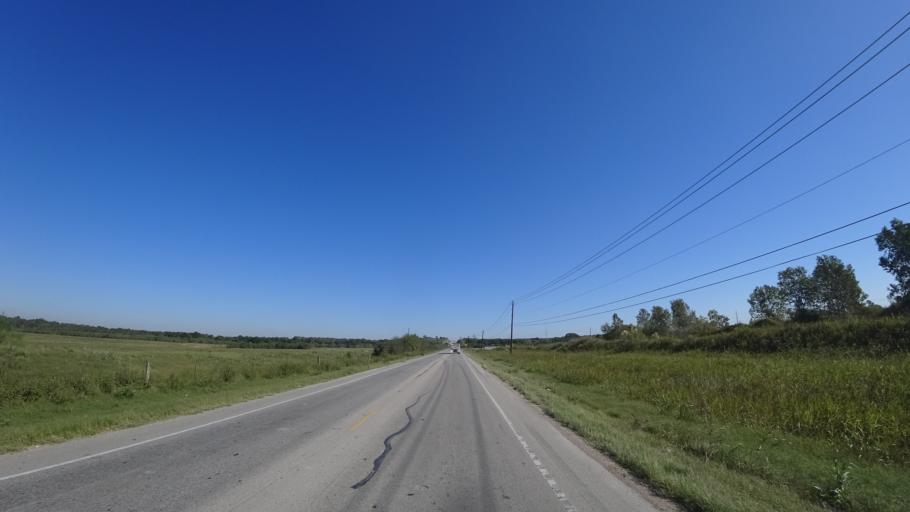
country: US
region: Texas
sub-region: Travis County
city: Hornsby Bend
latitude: 30.2512
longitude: -97.6155
